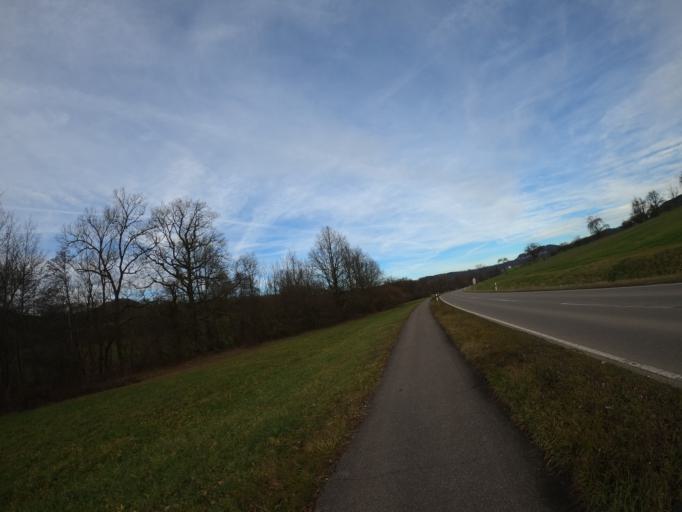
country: DE
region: Baden-Wuerttemberg
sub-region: Regierungsbezirk Stuttgart
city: Ottenbach
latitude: 48.7226
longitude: 9.7386
